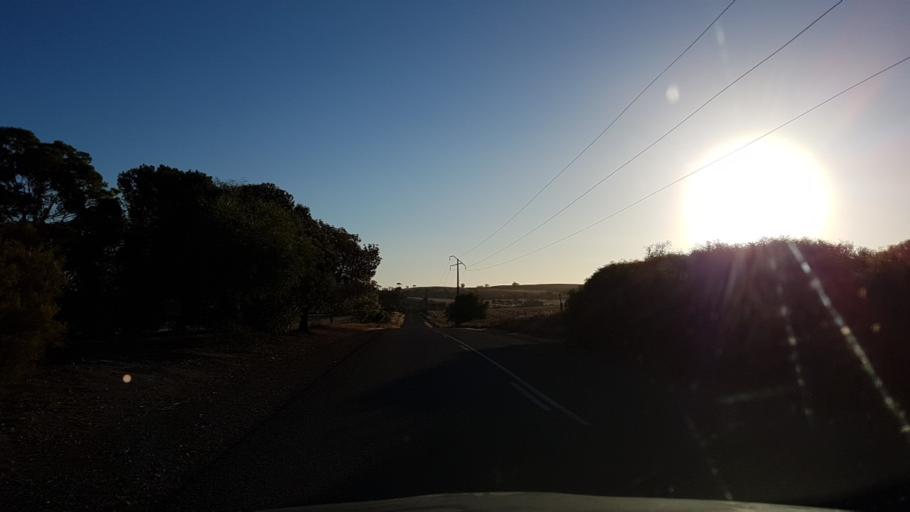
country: AU
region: South Australia
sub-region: Clare and Gilbert Valleys
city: Clare
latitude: -34.0212
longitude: 138.6978
